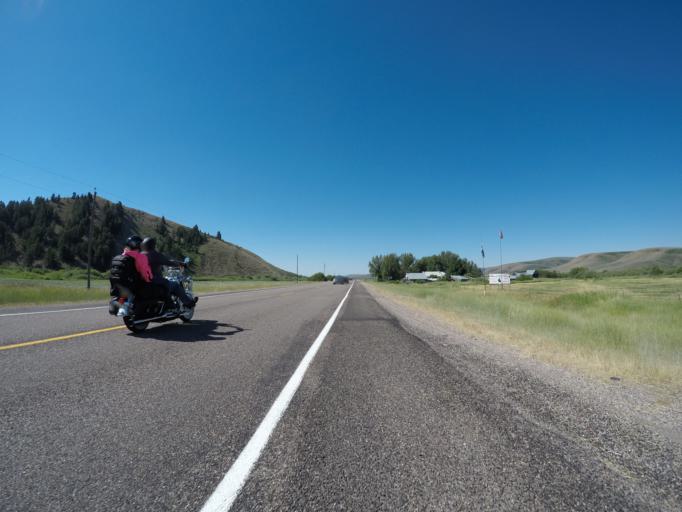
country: US
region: Idaho
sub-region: Bear Lake County
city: Montpelier
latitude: 42.3936
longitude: -111.0512
